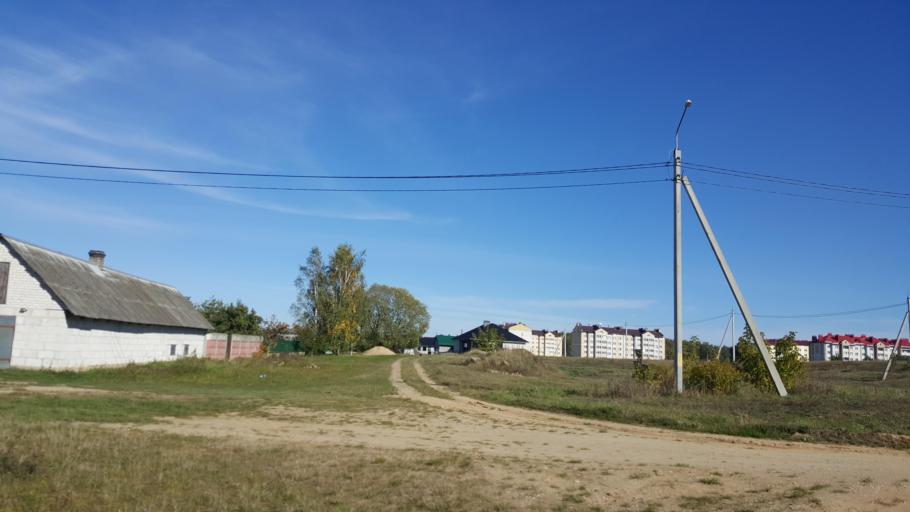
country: BY
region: Brest
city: Kamyanyets
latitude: 52.3873
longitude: 23.8110
